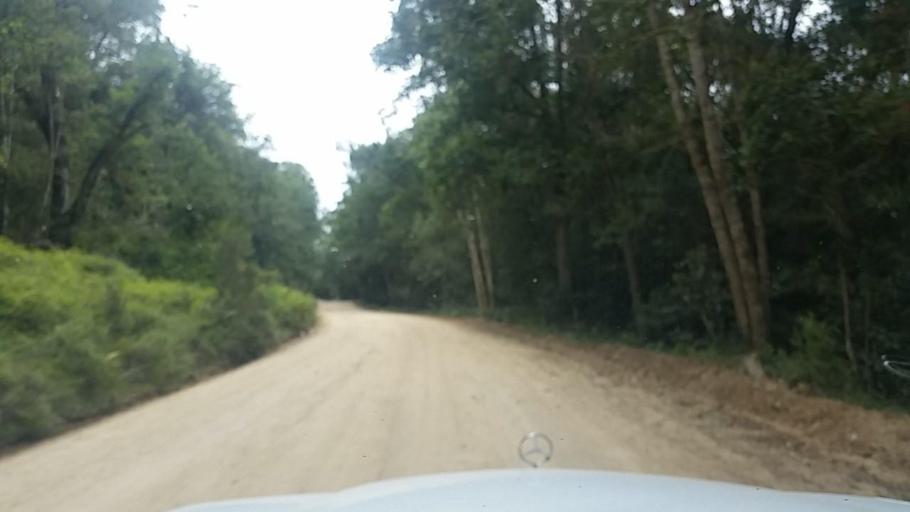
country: ZA
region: Western Cape
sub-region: Eden District Municipality
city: Knysna
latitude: -33.9457
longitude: 23.1558
